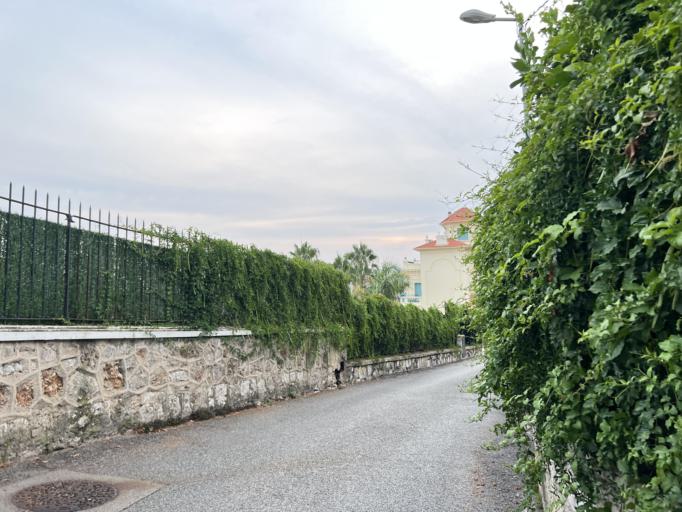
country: FR
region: Provence-Alpes-Cote d'Azur
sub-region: Departement des Alpes-Maritimes
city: Cap-d'Ail
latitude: 43.7203
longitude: 7.3904
